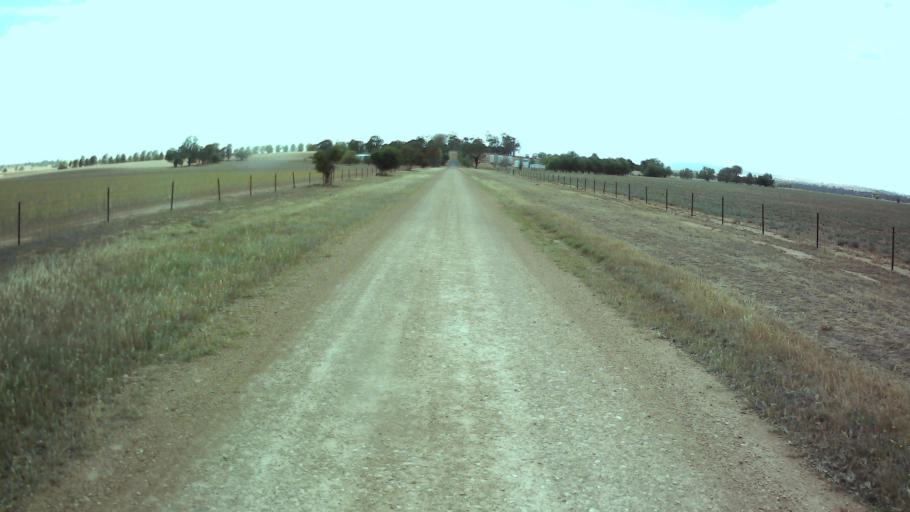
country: AU
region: New South Wales
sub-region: Weddin
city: Grenfell
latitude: -33.9955
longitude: 148.3056
